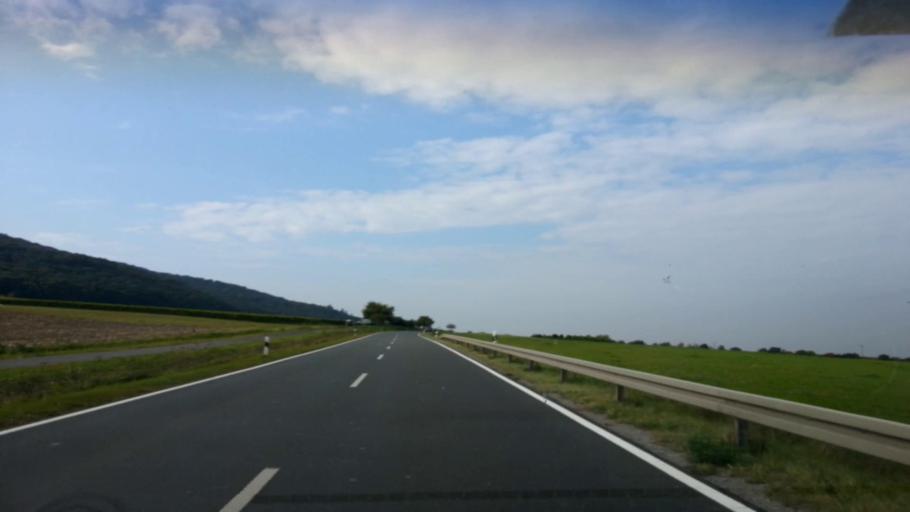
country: DE
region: Bavaria
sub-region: Regierungsbezirk Unterfranken
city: Wiesenbronn
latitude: 49.7374
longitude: 10.2872
